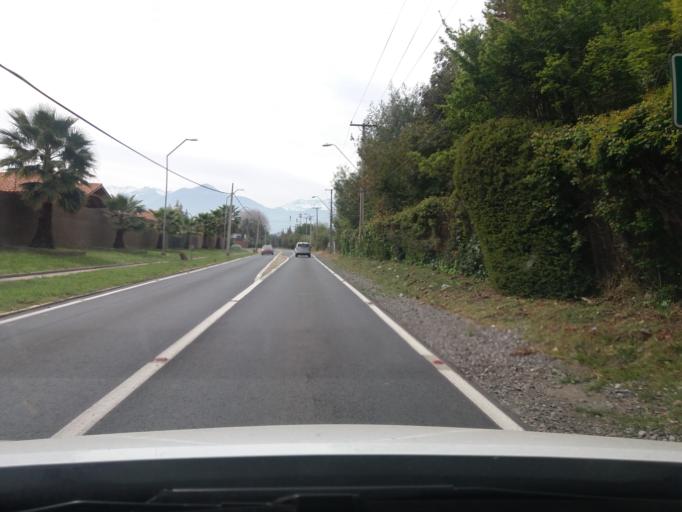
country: CL
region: Valparaiso
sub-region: Provincia de Los Andes
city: Los Andes
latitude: -32.8322
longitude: -70.6237
